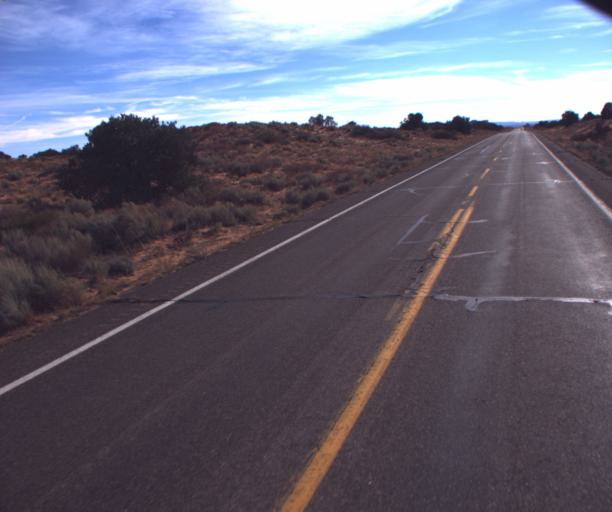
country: US
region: Arizona
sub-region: Coconino County
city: Kaibito
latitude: 36.6465
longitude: -111.2275
